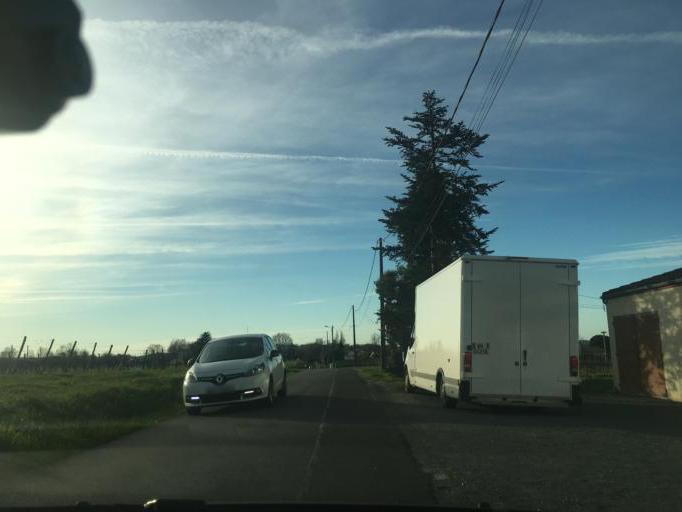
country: FR
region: Aquitaine
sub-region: Departement de la Gironde
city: Saint-Germain-du-Puch
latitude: 44.8614
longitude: -0.3207
